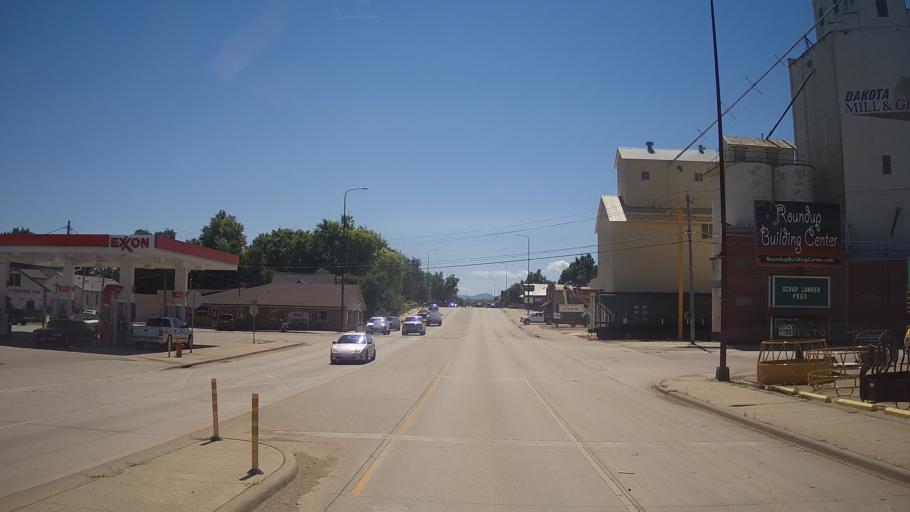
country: US
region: South Dakota
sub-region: Butte County
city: Belle Fourche
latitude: 44.6708
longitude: -103.8536
